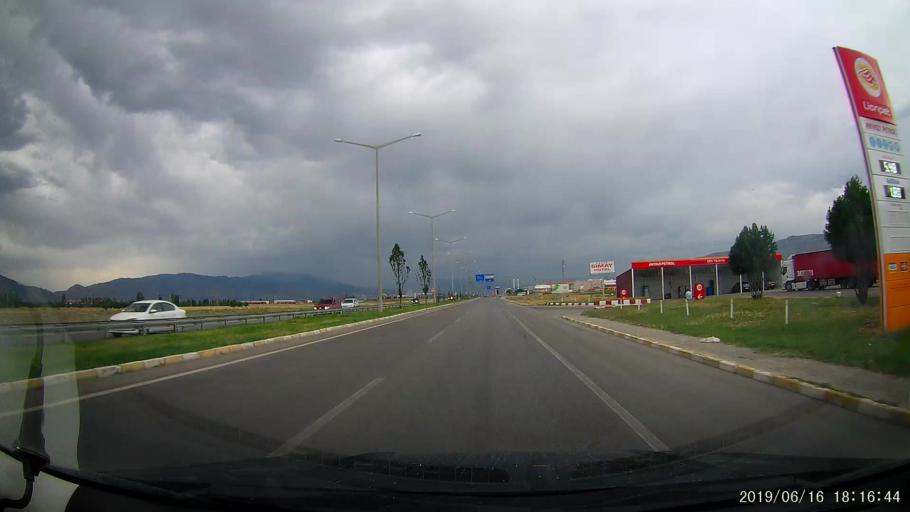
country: TR
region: Erzincan
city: Erzincan
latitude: 39.7301
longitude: 39.5436
